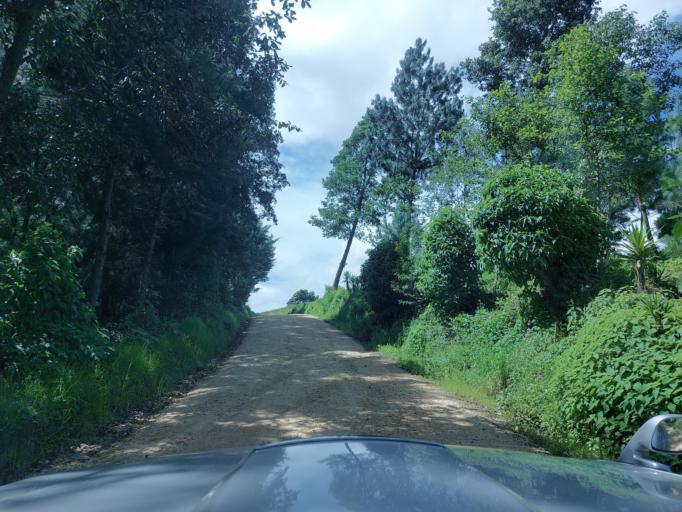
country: GT
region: Chimaltenango
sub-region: Municipio de San Juan Comalapa
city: Comalapa
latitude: 14.7579
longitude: -90.8772
